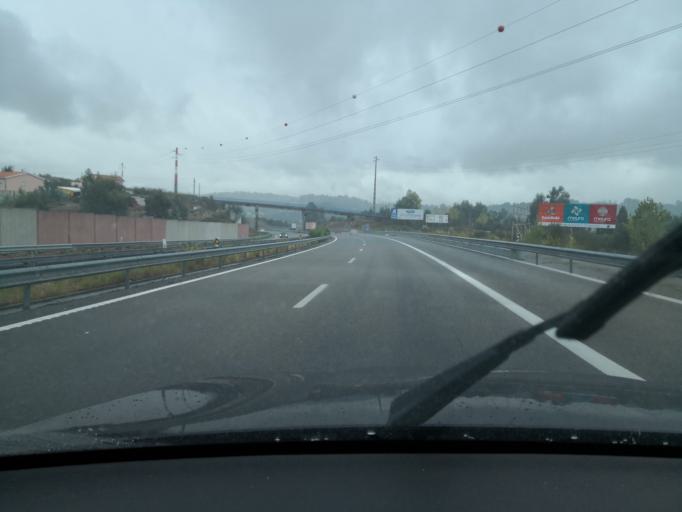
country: PT
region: Porto
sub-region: Pacos de Ferreira
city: Frazao
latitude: 41.2546
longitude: -8.4113
